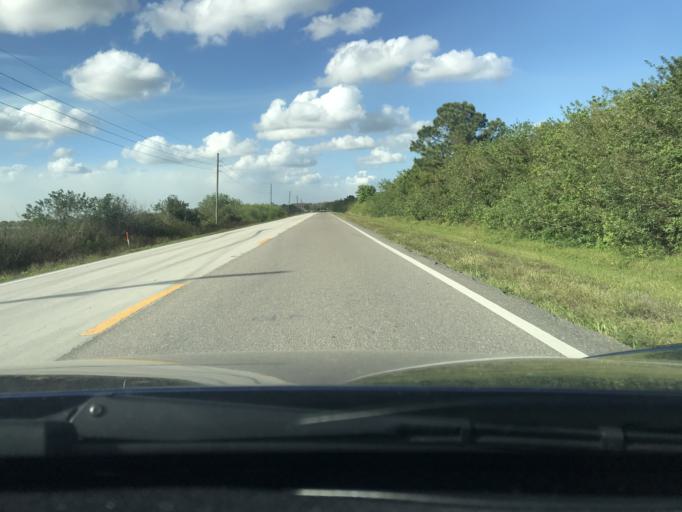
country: US
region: Florida
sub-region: Okeechobee County
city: Taylor Creek
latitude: 27.2799
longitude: -80.6958
